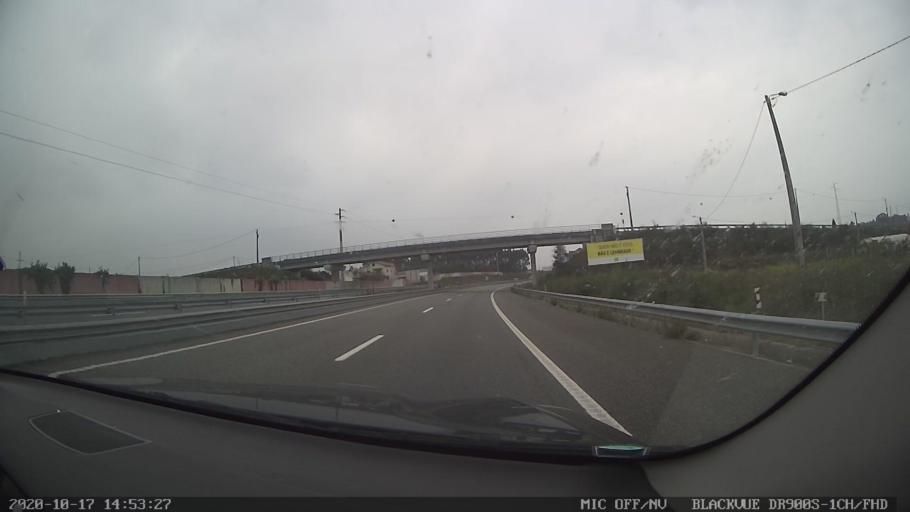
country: PT
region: Braga
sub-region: Barcelos
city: Vila Frescainha
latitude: 41.4998
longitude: -8.6636
